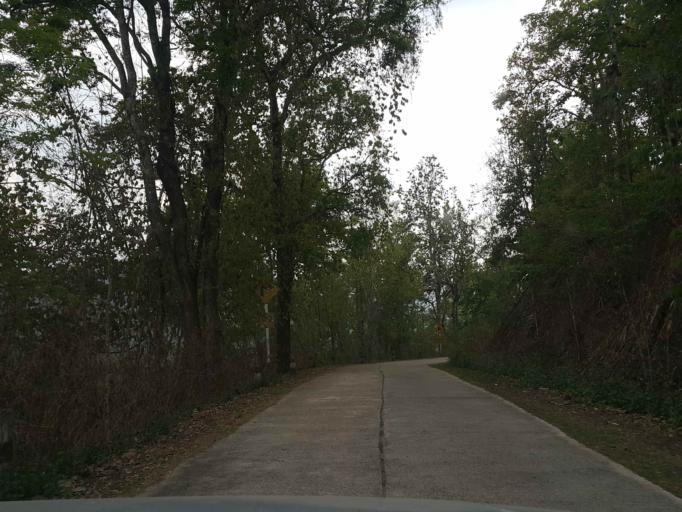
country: TH
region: Chiang Mai
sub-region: Amphoe Chiang Dao
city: Chiang Dao
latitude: 19.3846
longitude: 98.7724
